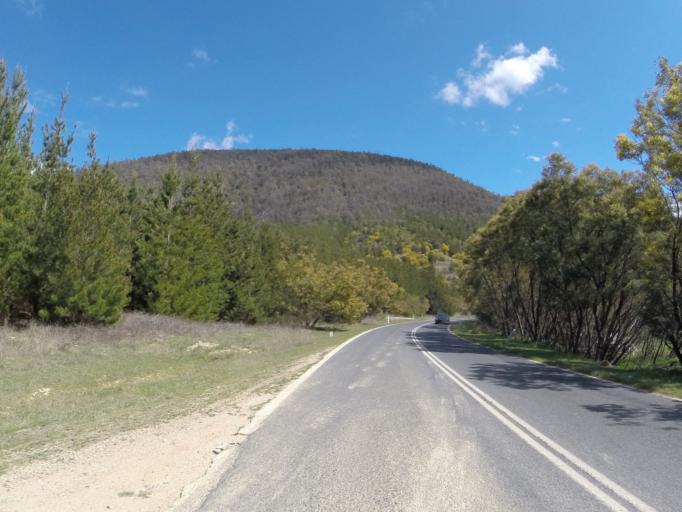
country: AU
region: Australian Capital Territory
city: Macquarie
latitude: -35.3669
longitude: 148.9545
